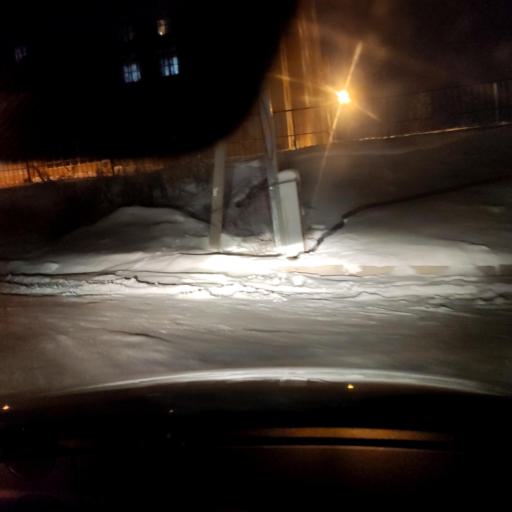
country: RU
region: Tatarstan
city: Stolbishchi
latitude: 55.7490
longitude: 49.2479
